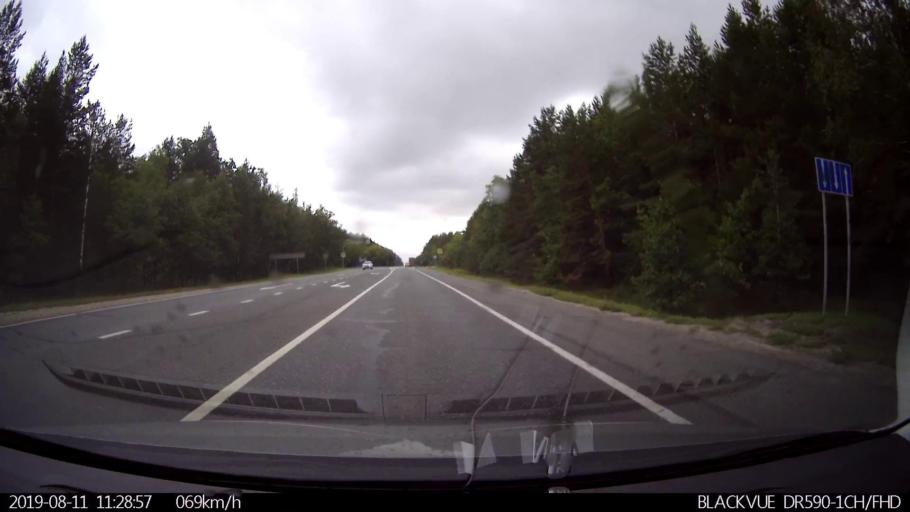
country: RU
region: Ulyanovsk
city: Krasnyy Gulyay
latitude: 54.0756
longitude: 48.2256
